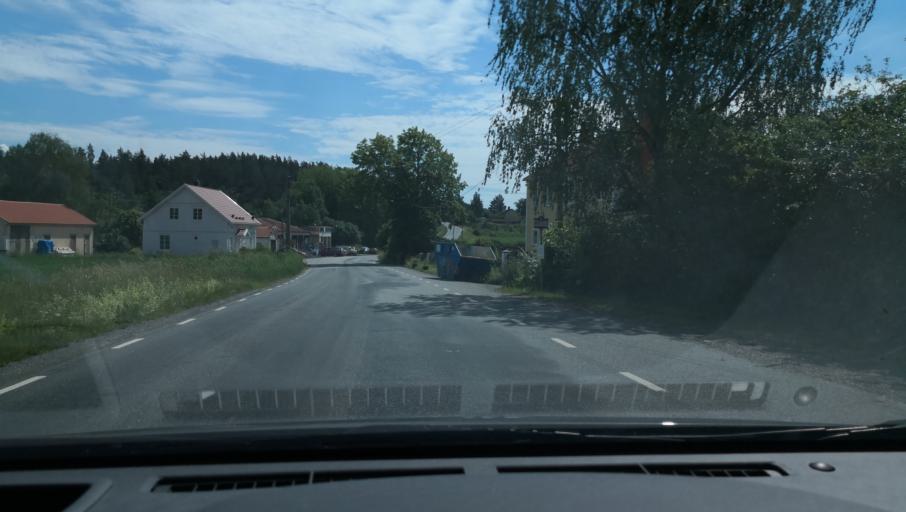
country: SE
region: Uppsala
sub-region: Habo Kommun
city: Balsta
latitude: 59.6634
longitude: 17.4489
